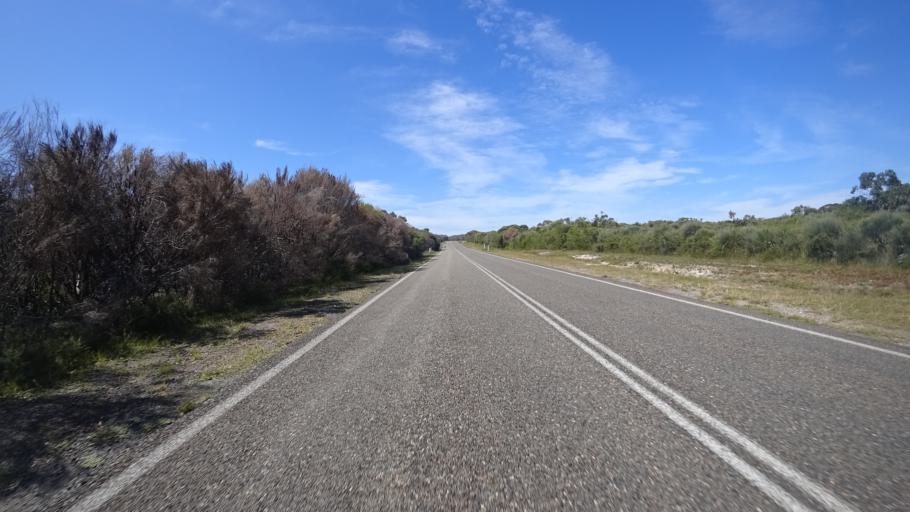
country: AU
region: New South Wales
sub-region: Shoalhaven Shire
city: Falls Creek
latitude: -35.1441
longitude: 150.7056
